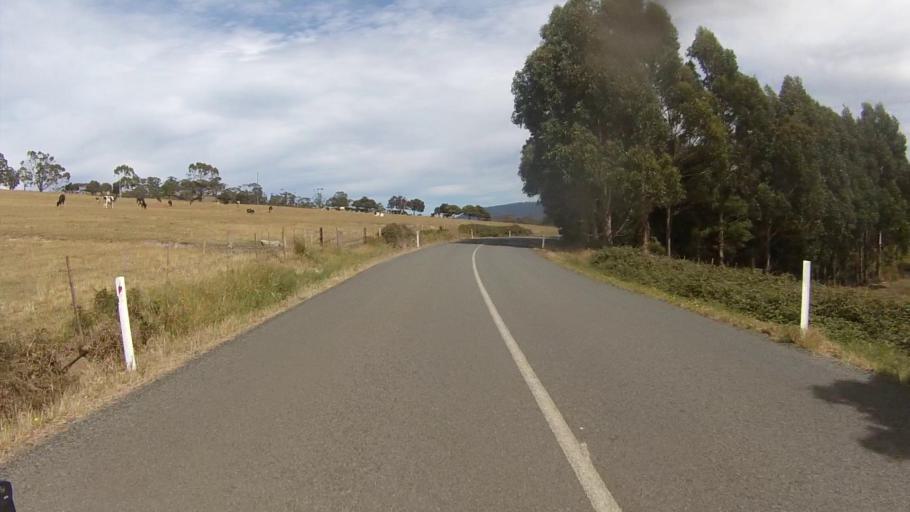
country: AU
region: Tasmania
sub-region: Sorell
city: Sorell
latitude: -42.8238
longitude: 147.8271
